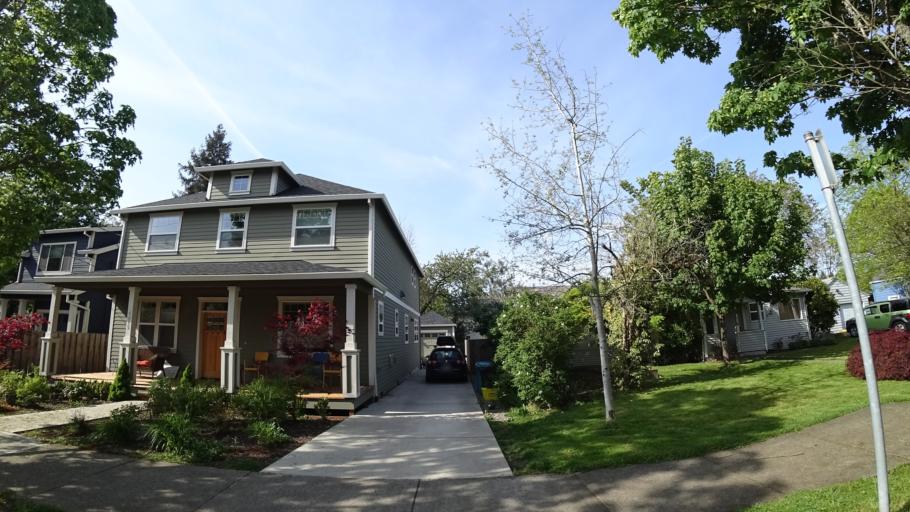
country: US
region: Oregon
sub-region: Clackamas County
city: Milwaukie
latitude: 45.4719
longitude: -122.6134
